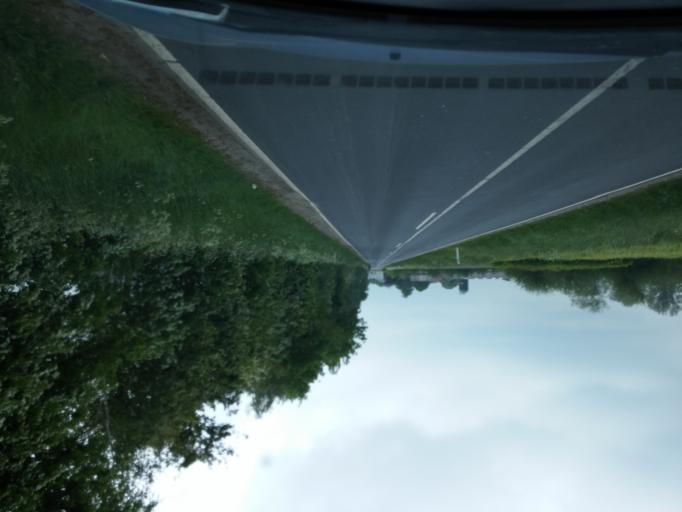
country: DK
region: South Denmark
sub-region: Kerteminde Kommune
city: Langeskov
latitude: 55.4045
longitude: 10.5763
